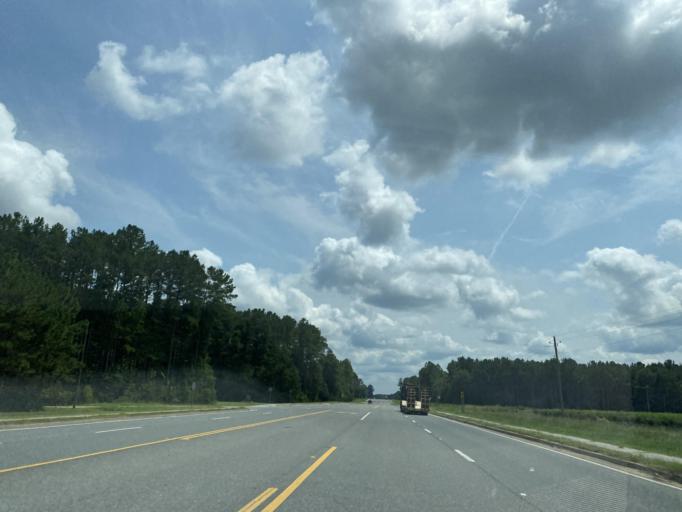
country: US
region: Georgia
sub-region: Ware County
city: Deenwood
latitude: 31.3480
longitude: -82.4638
